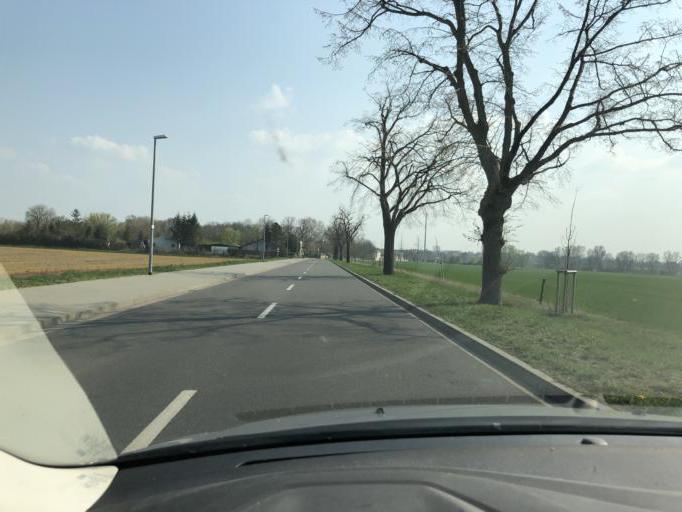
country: DE
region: Saxony-Anhalt
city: Grobers
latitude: 51.4412
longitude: 12.1150
